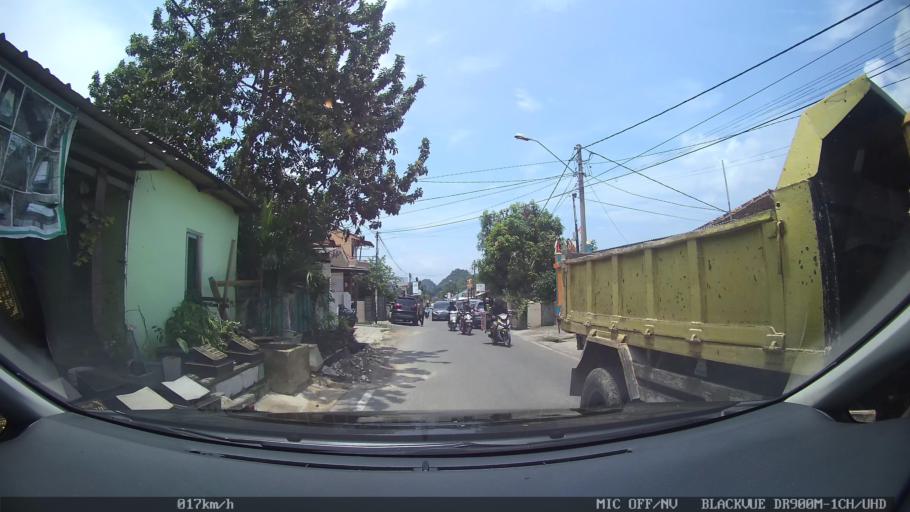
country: ID
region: Lampung
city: Kedaton
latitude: -5.3878
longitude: 105.2496
